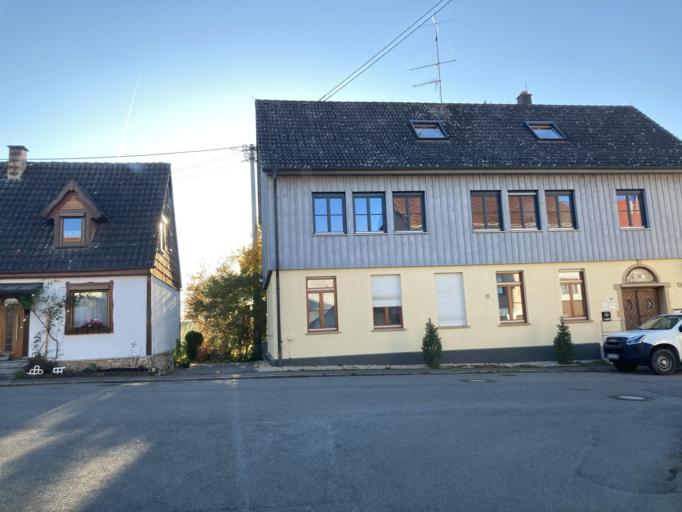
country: DE
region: Baden-Wuerttemberg
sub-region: Tuebingen Region
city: Rottenburg
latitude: 48.4329
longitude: 8.9384
